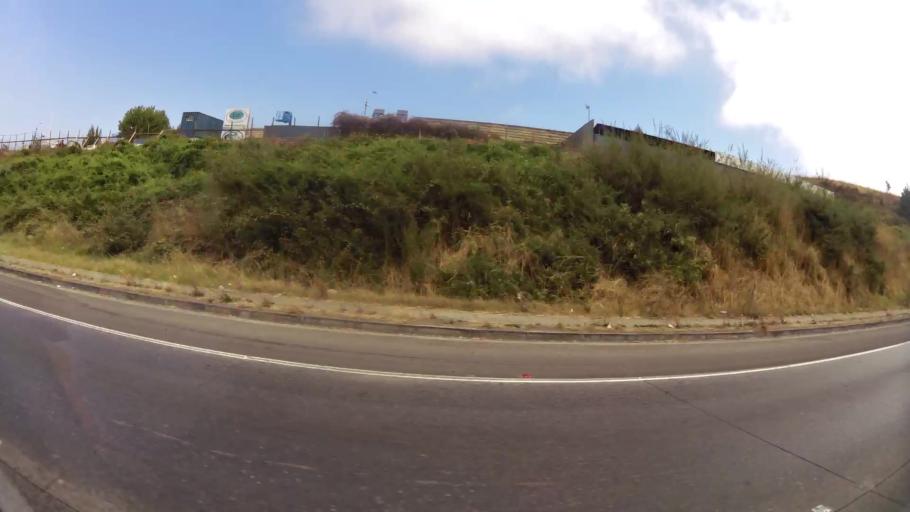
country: CL
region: Biobio
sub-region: Provincia de Concepcion
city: Concepcion
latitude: -36.8001
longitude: -73.0437
